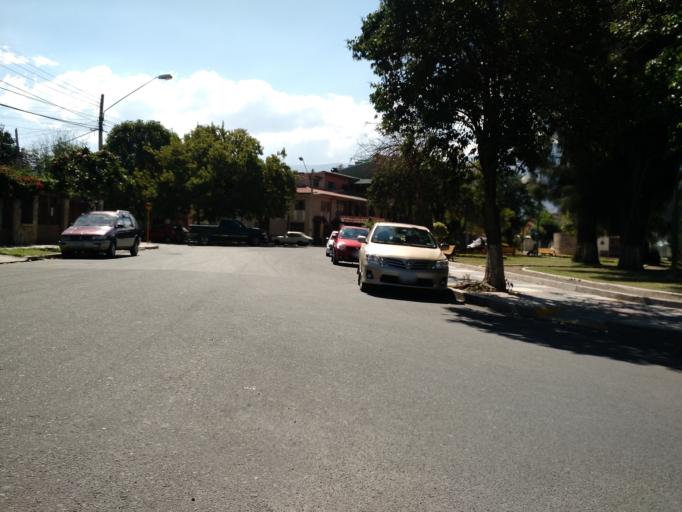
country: BO
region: Cochabamba
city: Cochabamba
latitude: -17.3907
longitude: -66.1694
